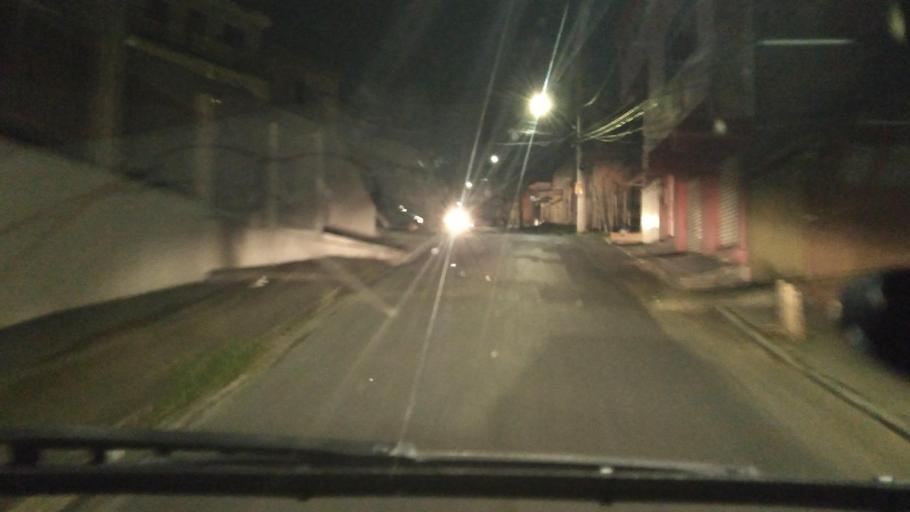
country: BR
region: Minas Gerais
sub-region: Belo Horizonte
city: Belo Horizonte
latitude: -19.8980
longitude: -43.9510
